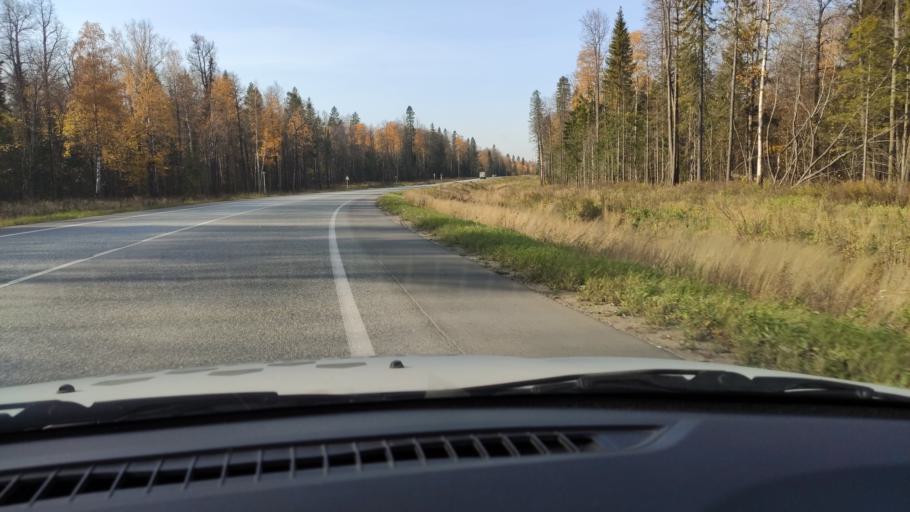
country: RU
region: Perm
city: Novyye Lyady
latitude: 58.0281
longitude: 56.5024
